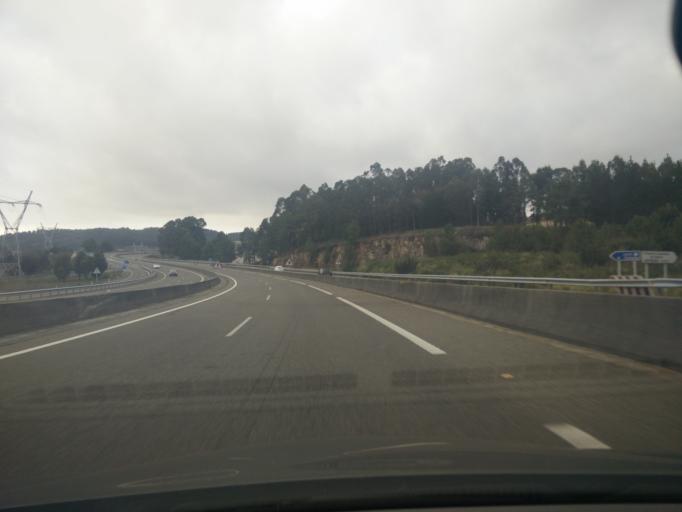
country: ES
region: Galicia
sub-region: Provincia da Coruna
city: Arteixo
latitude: 43.3070
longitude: -8.4745
